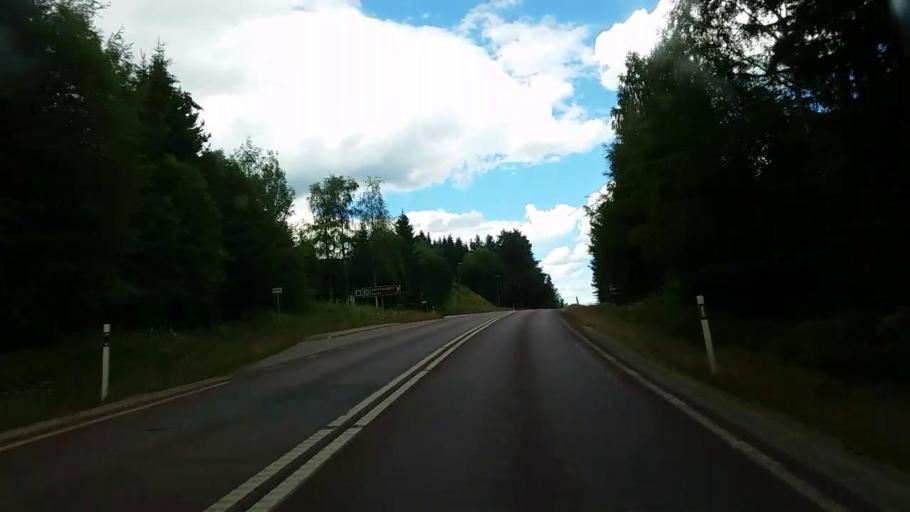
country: SE
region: Gaevleborg
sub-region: Ljusdals Kommun
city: Jaervsoe
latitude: 61.6832
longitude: 16.1460
